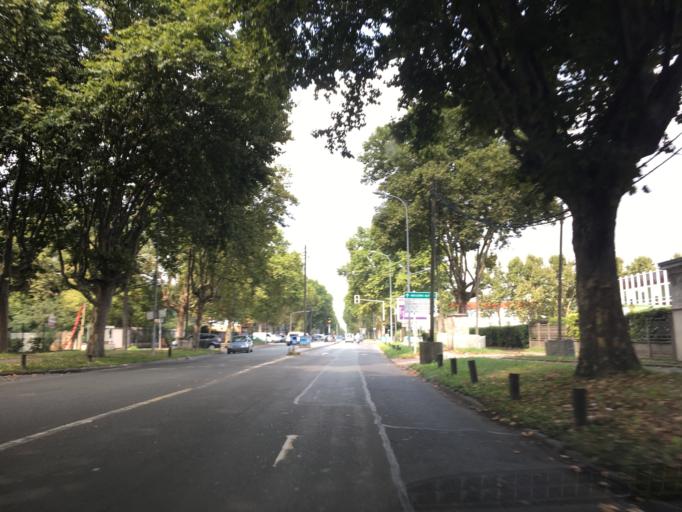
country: FR
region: Ile-de-France
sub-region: Departement du Val-de-Marne
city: Choisy-le-Roi
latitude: 48.7864
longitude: 2.4360
